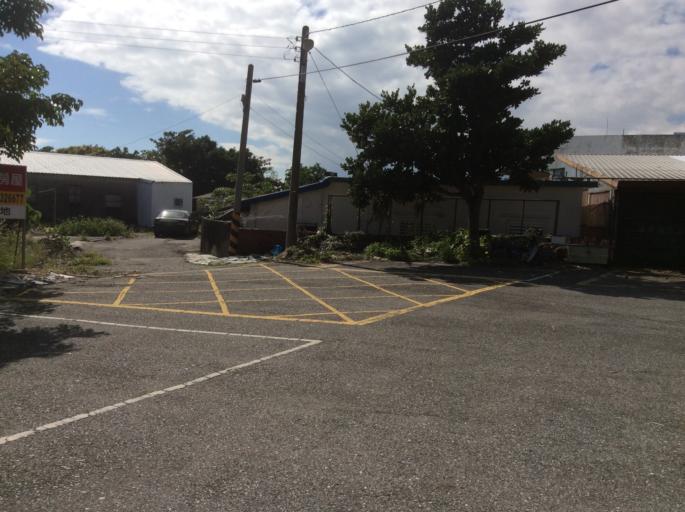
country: TW
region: Taiwan
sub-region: Taitung
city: Taitung
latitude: 23.3149
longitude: 121.4521
